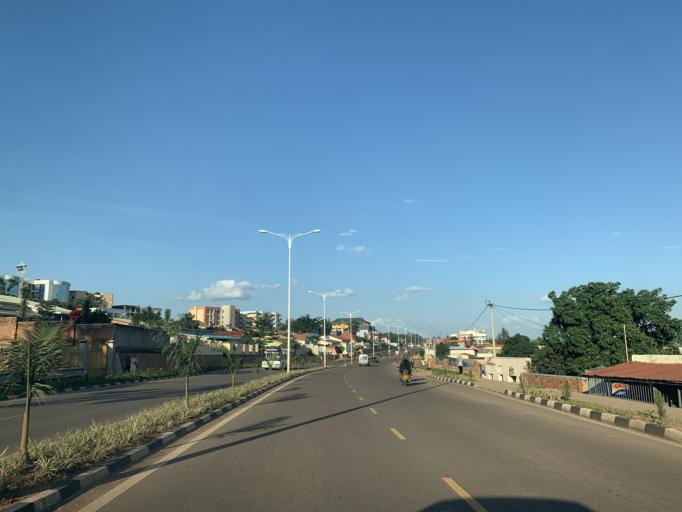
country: RW
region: Kigali
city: Kigali
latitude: -1.9627
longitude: 30.1094
